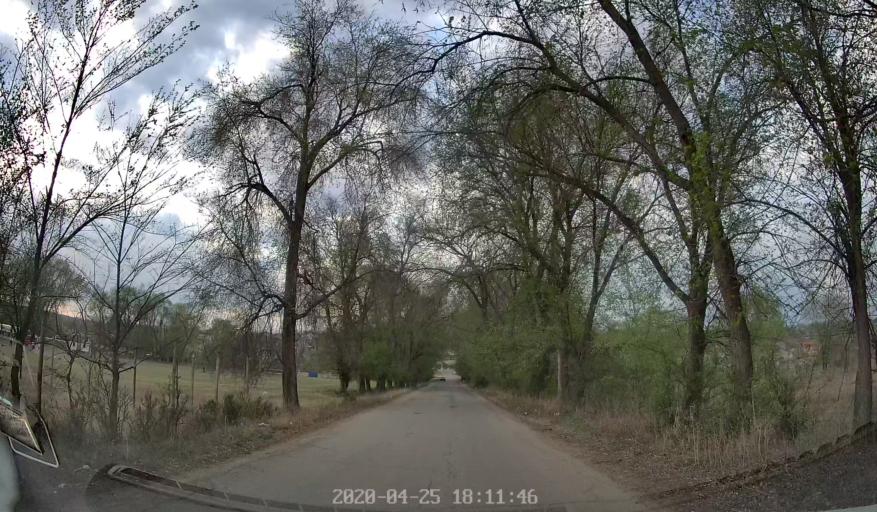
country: MD
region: Chisinau
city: Vadul lui Voda
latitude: 47.1405
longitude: 29.0689
